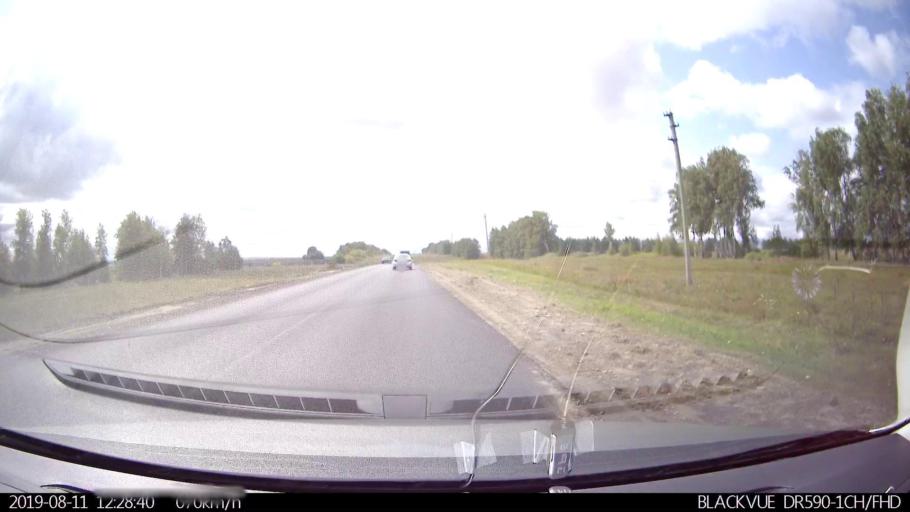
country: RU
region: Ulyanovsk
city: Ignatovka
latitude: 53.8415
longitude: 47.9097
